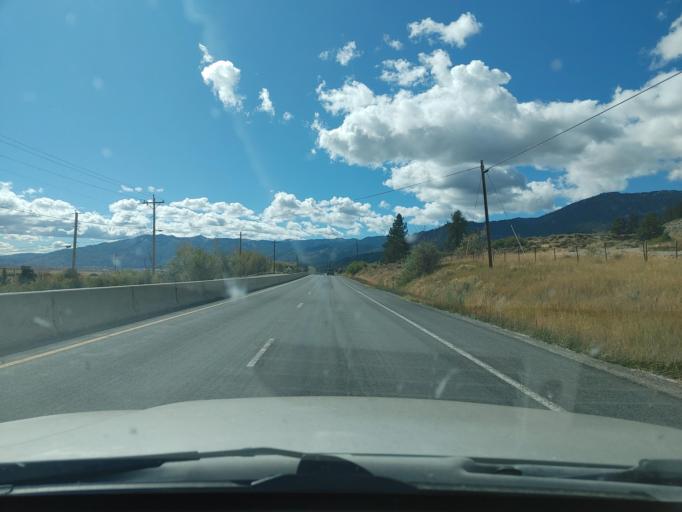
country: US
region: Nevada
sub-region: Carson City
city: Carson City
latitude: 39.3188
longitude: -119.8186
